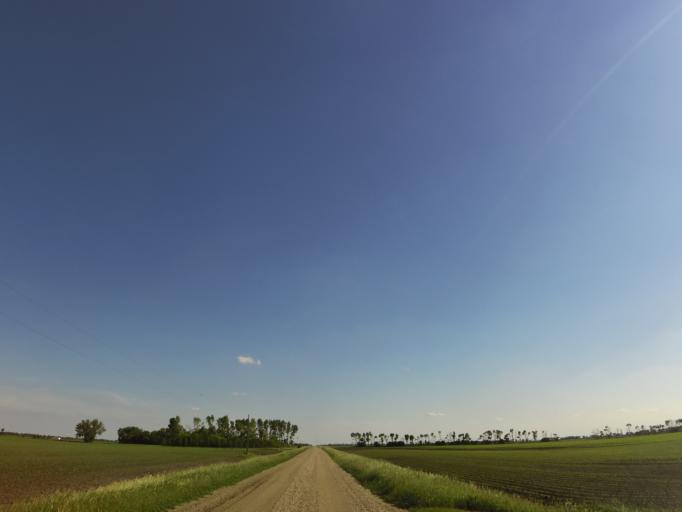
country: US
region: North Dakota
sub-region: Walsh County
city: Grafton
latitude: 48.3501
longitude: -97.2330
